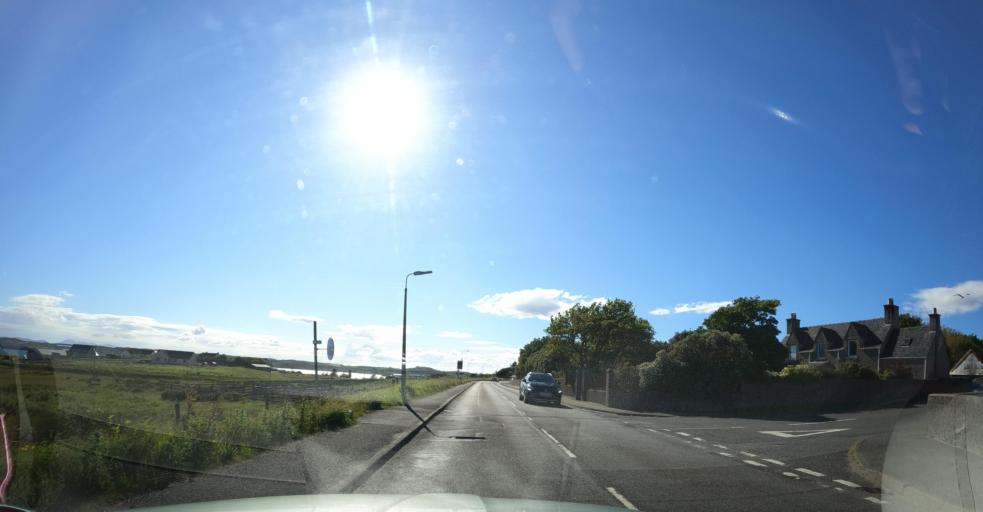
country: GB
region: Scotland
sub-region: Eilean Siar
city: Stornoway
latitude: 58.2035
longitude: -6.3481
